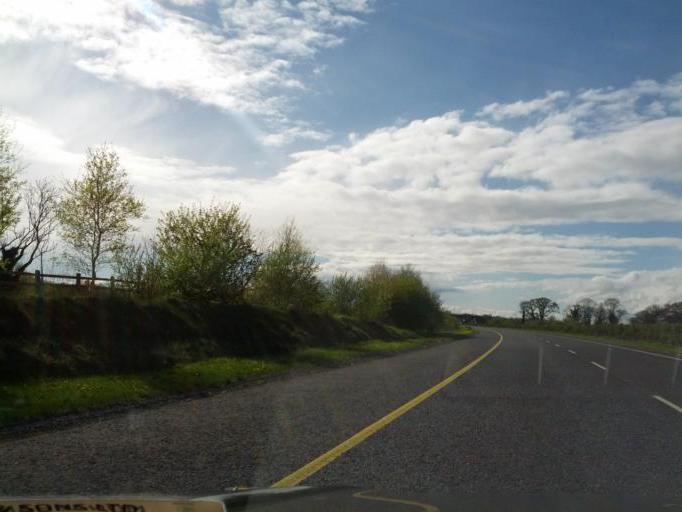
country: IE
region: Leinster
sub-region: An Mhi
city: Longwood
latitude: 53.4246
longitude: -6.9197
